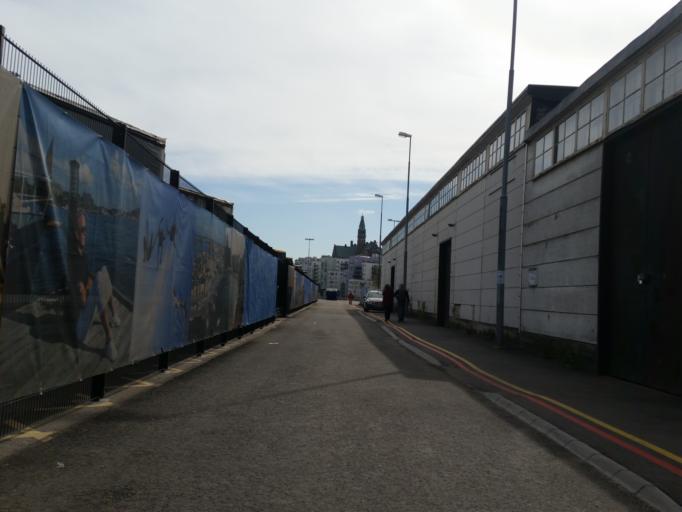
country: SE
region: Stockholm
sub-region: Stockholms Kommun
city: OEstermalm
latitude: 59.3156
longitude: 18.1043
